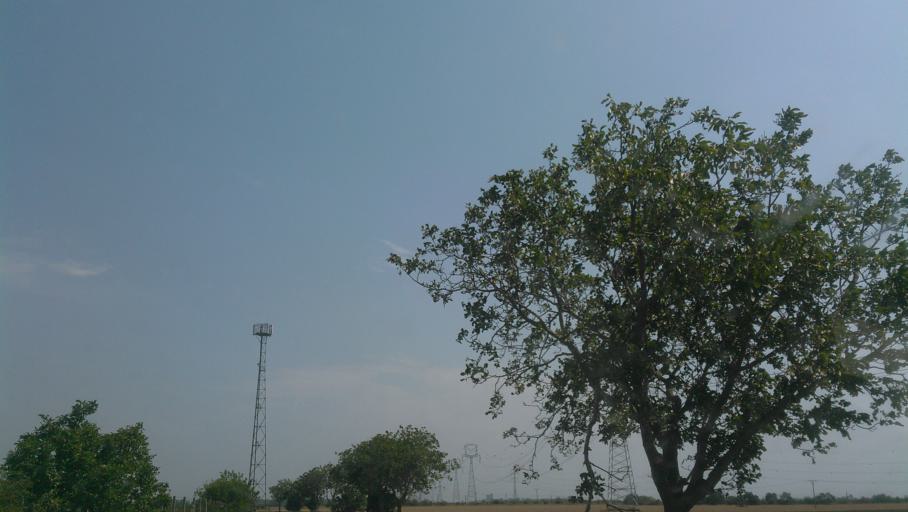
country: SK
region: Trnavsky
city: Samorin
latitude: 48.0641
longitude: 17.4198
